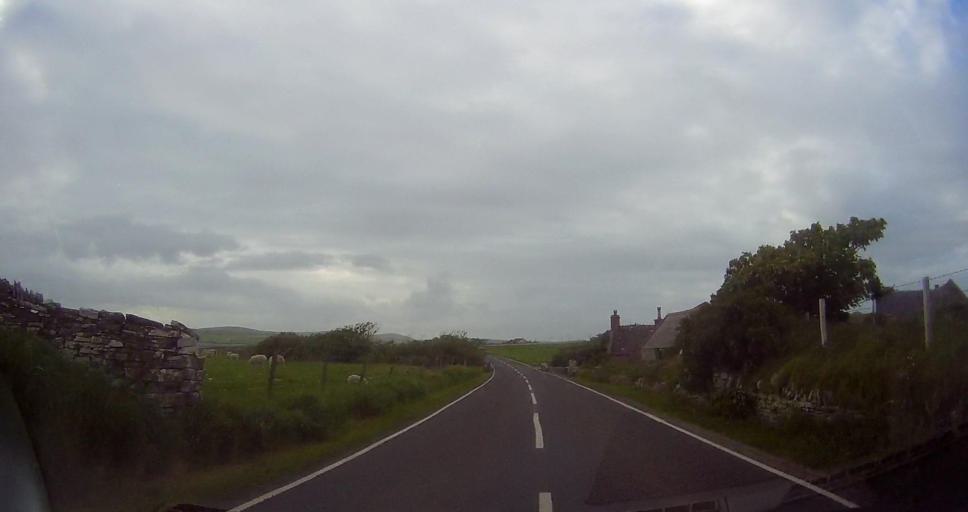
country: GB
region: Scotland
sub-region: Orkney Islands
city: Stromness
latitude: 58.9679
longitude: -3.2274
